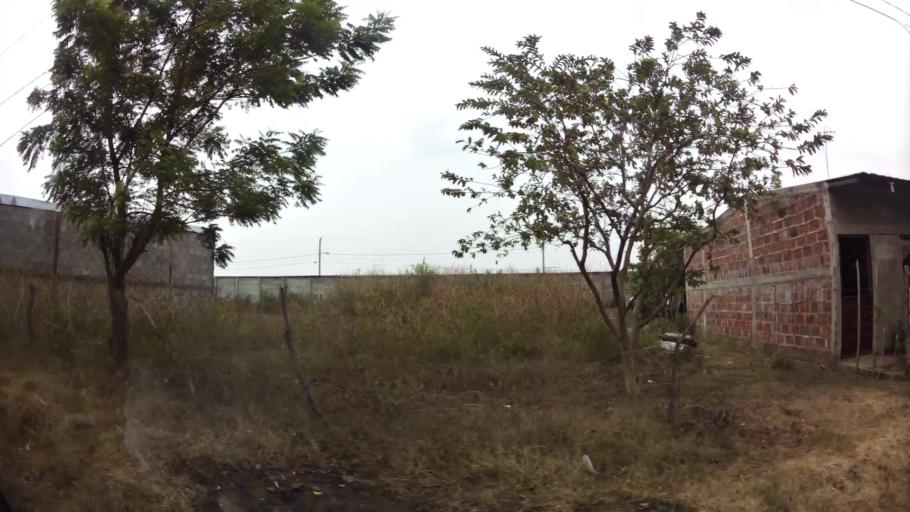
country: NI
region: Chinandega
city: Chinandega
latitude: 12.6257
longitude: -87.1118
